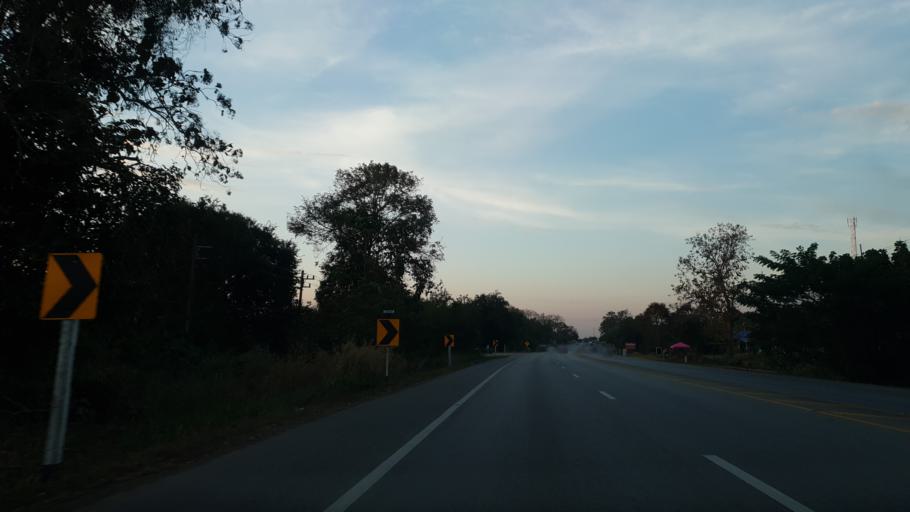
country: TH
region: Phitsanulok
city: Wang Thong
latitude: 16.8723
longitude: 100.6657
